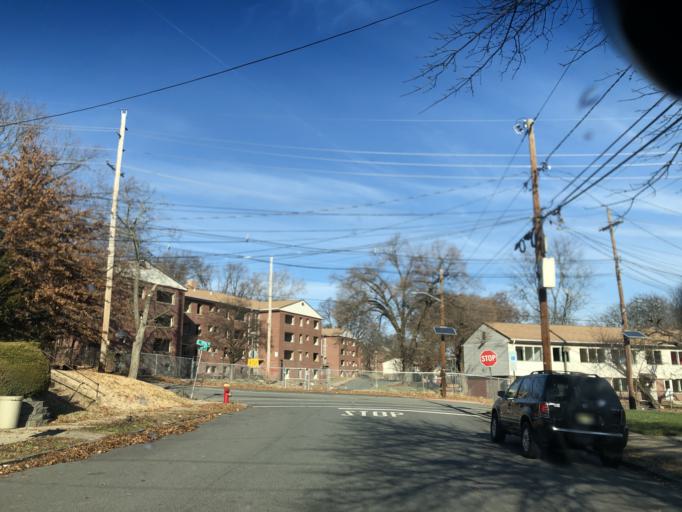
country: US
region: New Jersey
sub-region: Bergen County
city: Fair Lawn
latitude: 40.9291
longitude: -74.1446
